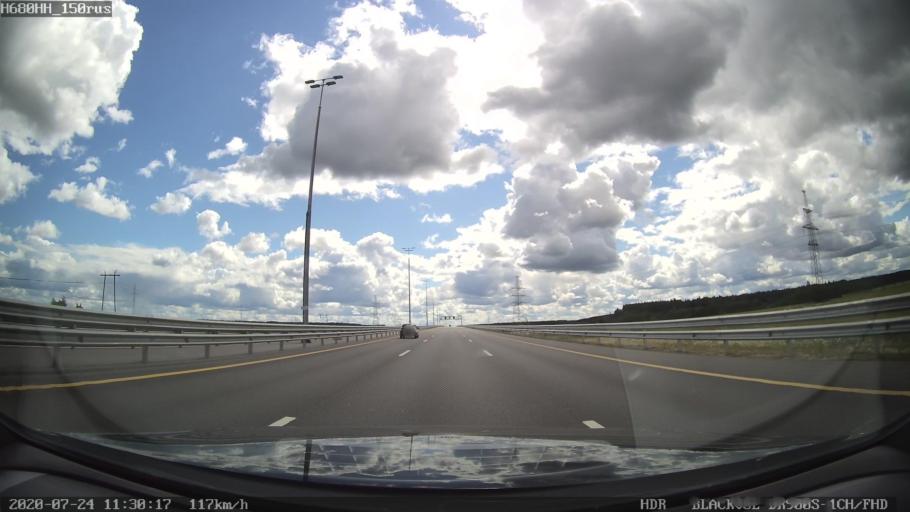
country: RU
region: Leningrad
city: Krasnyy Bor
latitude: 59.6710
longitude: 30.6099
